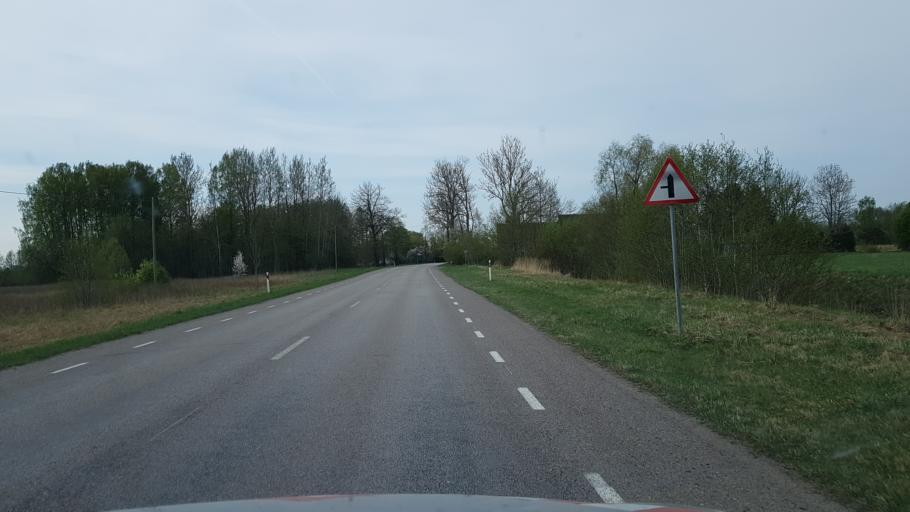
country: EE
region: Paernumaa
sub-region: Audru vald
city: Audru
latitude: 58.3727
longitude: 24.2695
